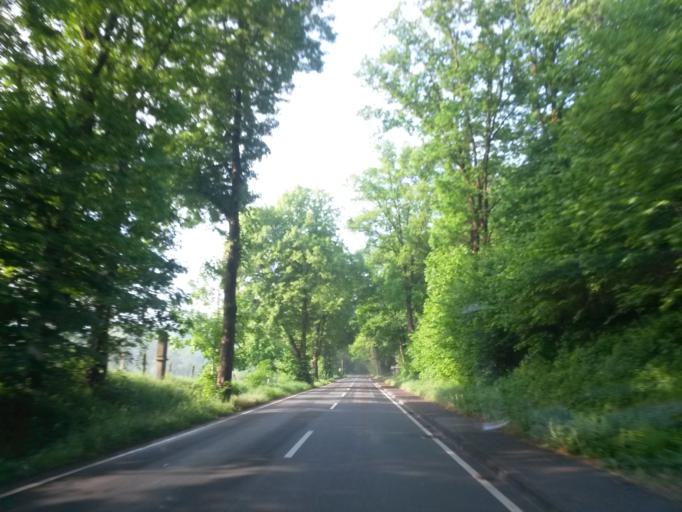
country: DE
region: North Rhine-Westphalia
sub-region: Regierungsbezirk Koln
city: Much
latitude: 50.8971
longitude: 7.4073
